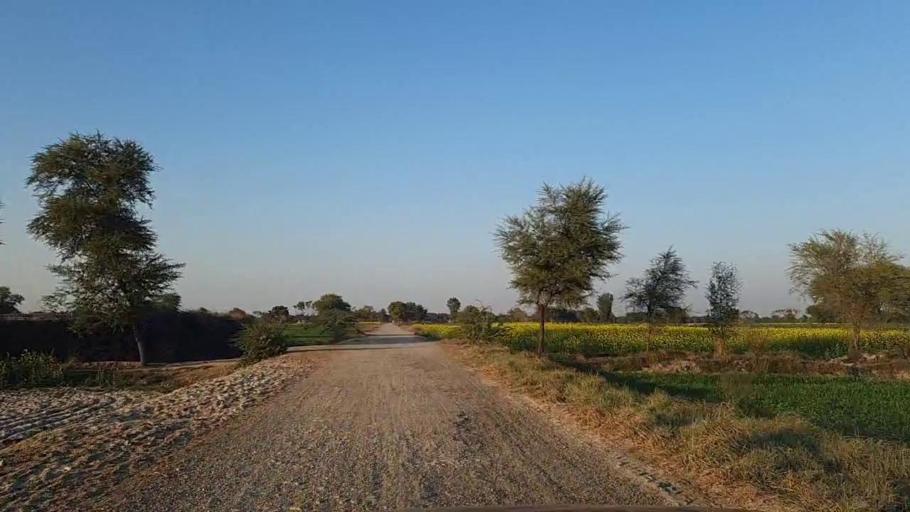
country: PK
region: Sindh
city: Nawabshah
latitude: 26.2341
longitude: 68.3381
